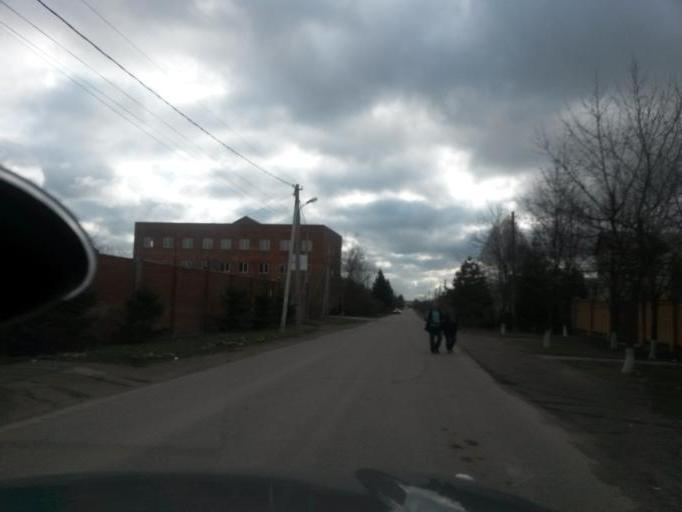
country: RU
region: Moskovskaya
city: Alekseyevka
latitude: 55.6020
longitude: 37.8190
